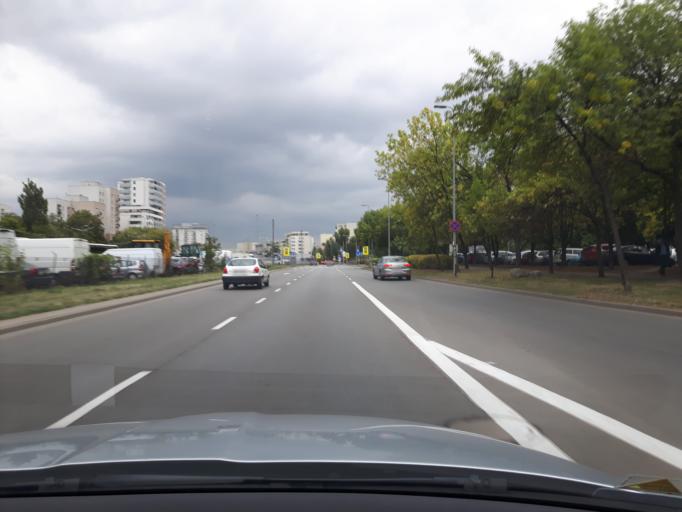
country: PL
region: Masovian Voivodeship
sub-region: Warszawa
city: Ursynow
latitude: 52.1649
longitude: 21.0268
